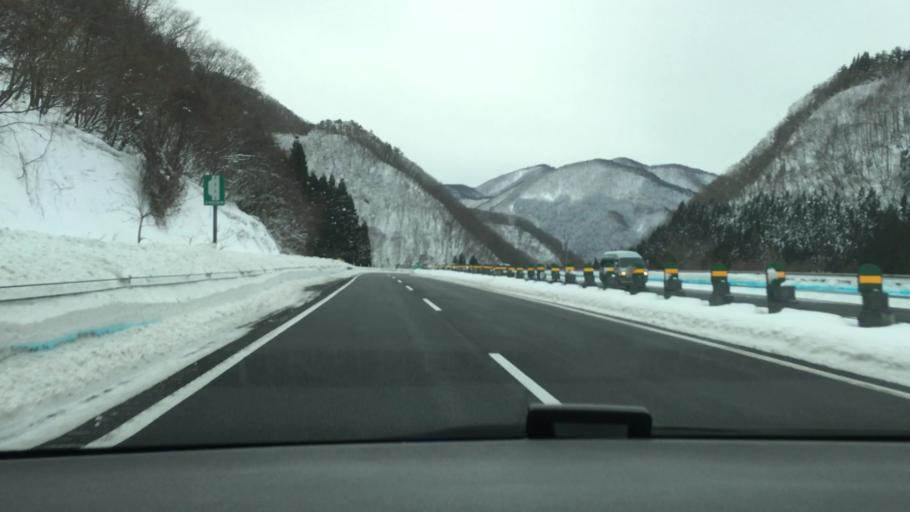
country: JP
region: Akita
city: Hanawa
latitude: 40.1236
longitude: 140.9074
